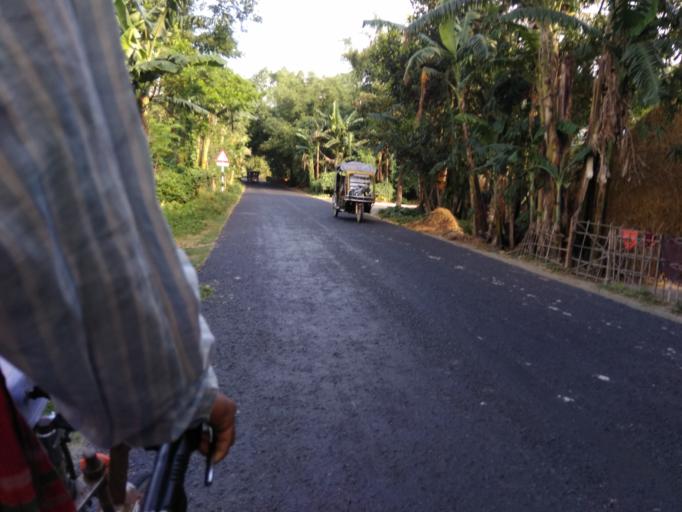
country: BD
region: Rangpur Division
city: Rangpur
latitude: 25.8329
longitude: 89.1173
